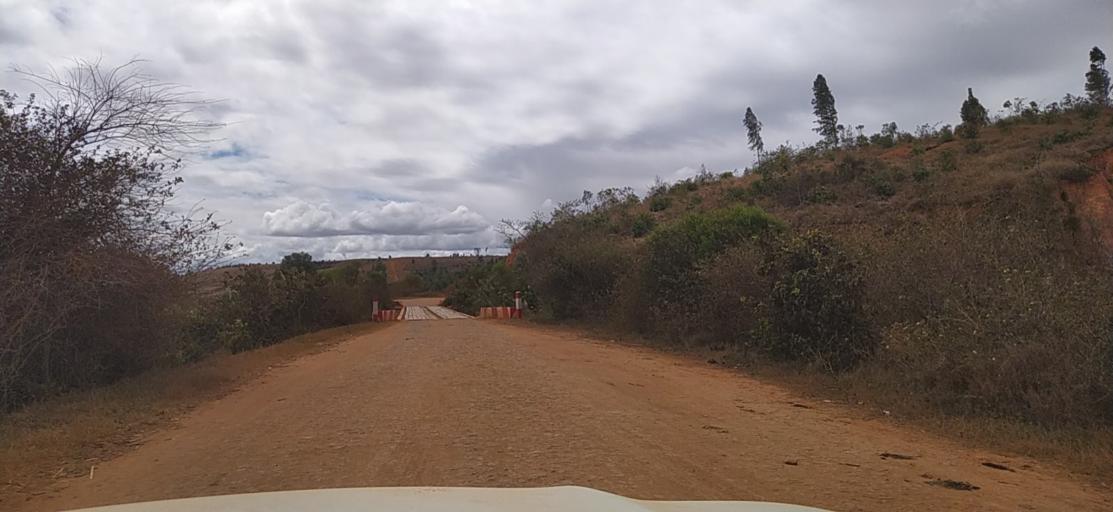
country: MG
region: Alaotra Mangoro
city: Ambatondrazaka
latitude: -18.0027
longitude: 48.2629
